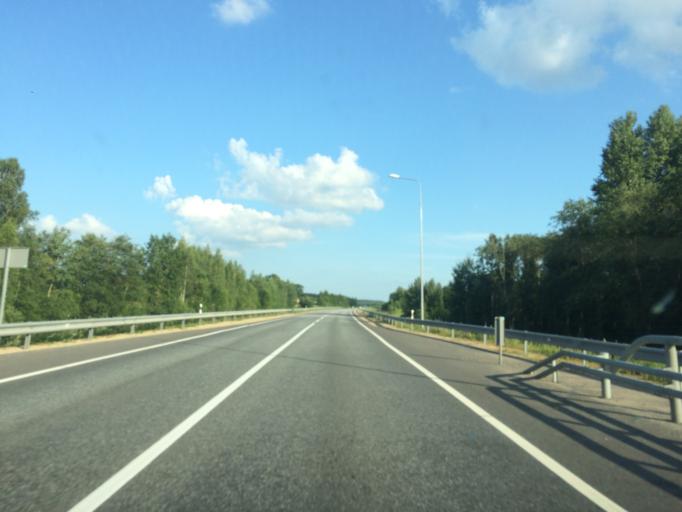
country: LV
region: Skriveri
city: Skriveri
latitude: 56.7630
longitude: 25.1031
